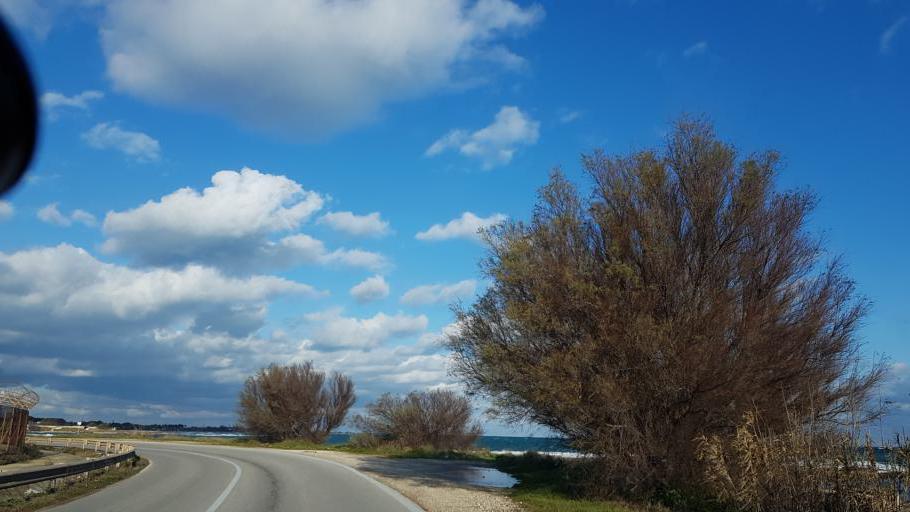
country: IT
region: Apulia
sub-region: Provincia di Brindisi
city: Materdomini
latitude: 40.6634
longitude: 17.9569
